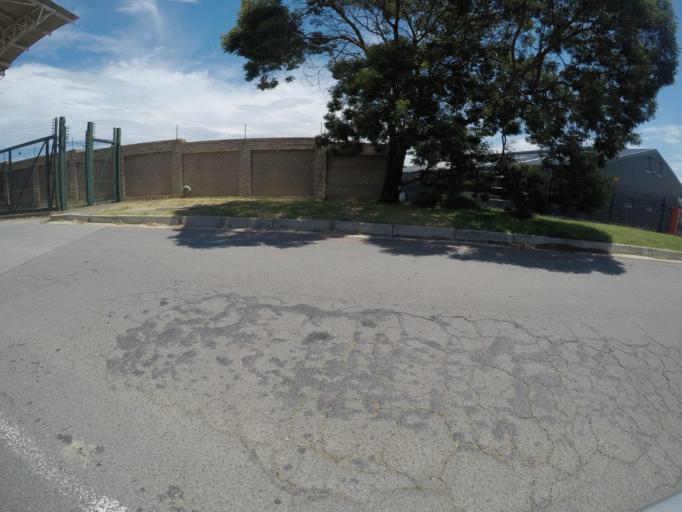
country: ZA
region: Eastern Cape
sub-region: Buffalo City Metropolitan Municipality
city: East London
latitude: -33.0364
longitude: 27.8412
